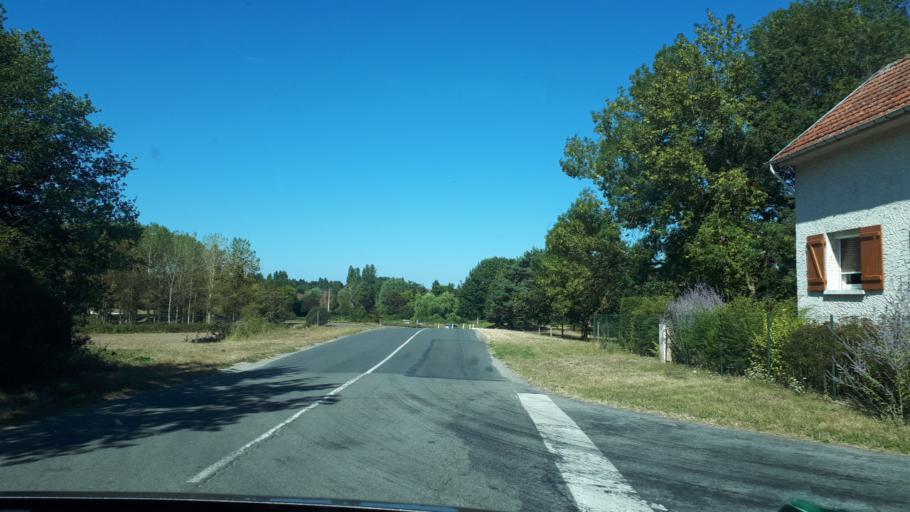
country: FR
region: Centre
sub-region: Departement du Loiret
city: Coullons
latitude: 47.6234
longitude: 2.5018
